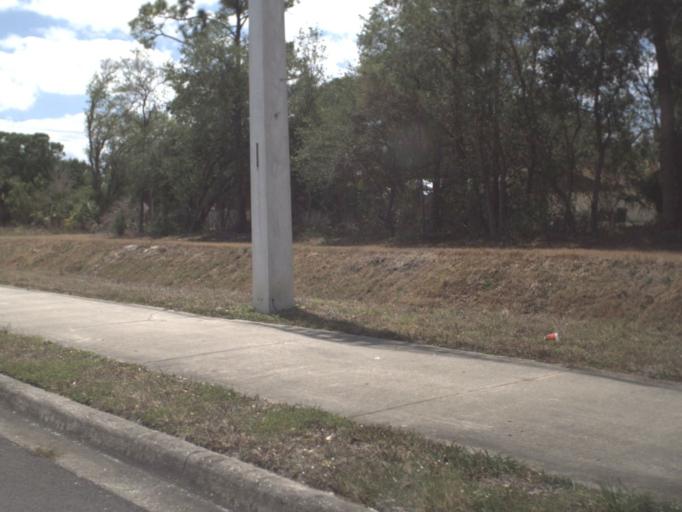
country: US
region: Florida
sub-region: Brevard County
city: Palm Bay
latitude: 28.0055
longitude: -80.6220
